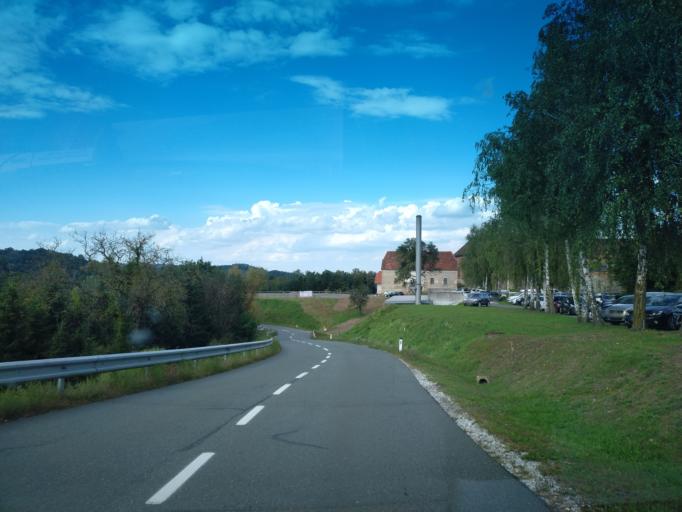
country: AT
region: Styria
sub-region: Politischer Bezirk Leibnitz
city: Leibnitz
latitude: 46.7818
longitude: 15.5227
